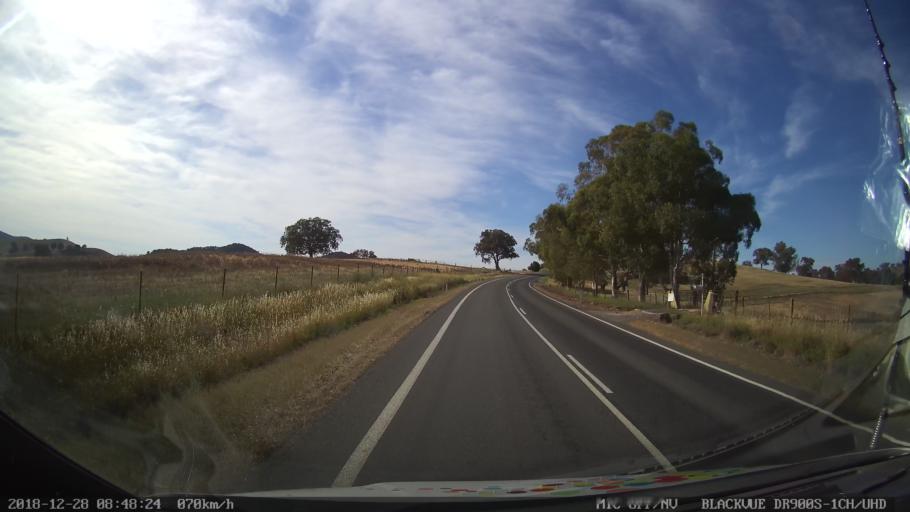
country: AU
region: New South Wales
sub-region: Upper Lachlan Shire
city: Crookwell
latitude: -34.0366
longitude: 149.3367
